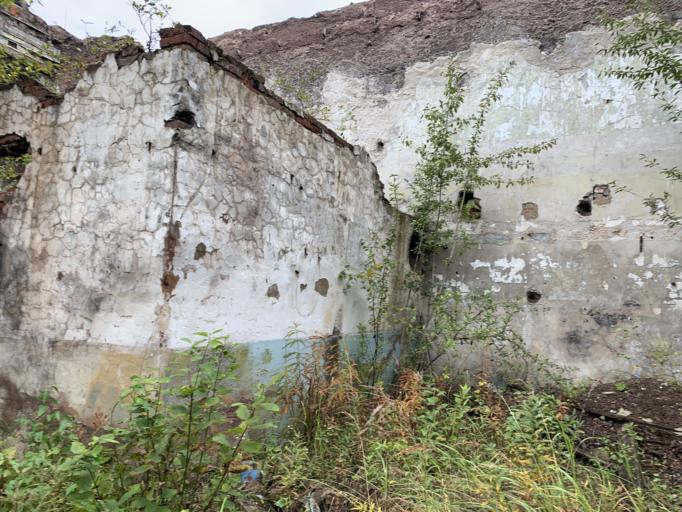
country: RU
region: Perm
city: Gubakha
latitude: 58.8720
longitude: 57.6036
